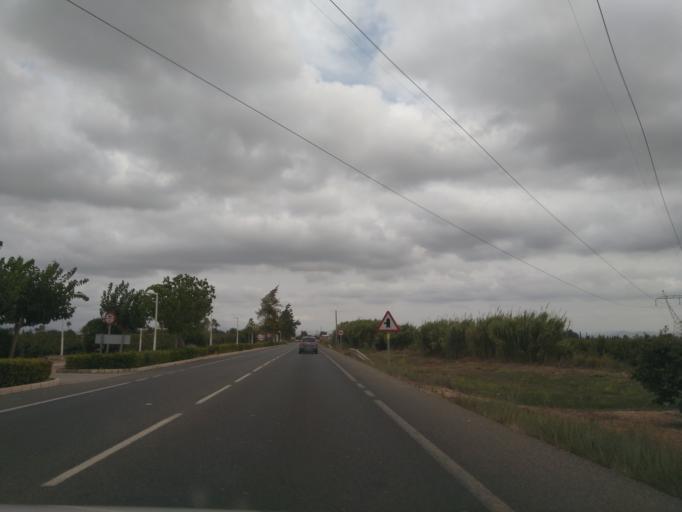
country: ES
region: Valencia
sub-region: Provincia de Valencia
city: L'Alcudia
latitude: 39.2113
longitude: -0.5123
